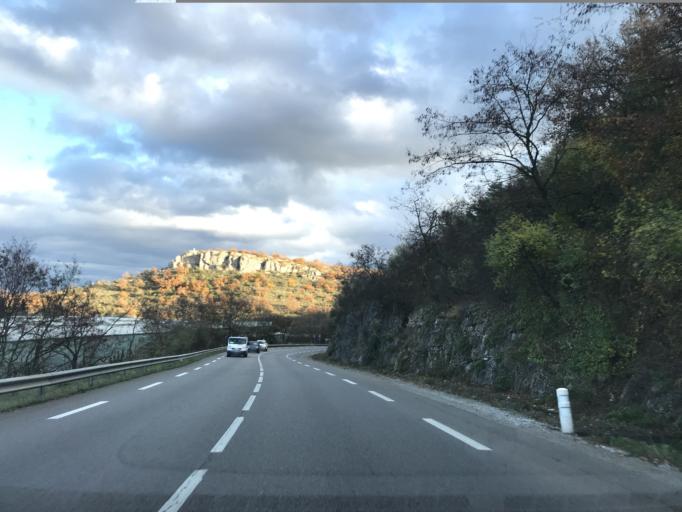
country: FR
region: Rhone-Alpes
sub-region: Departement de l'Ardeche
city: Alissas
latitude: 44.7115
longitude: 4.6201
